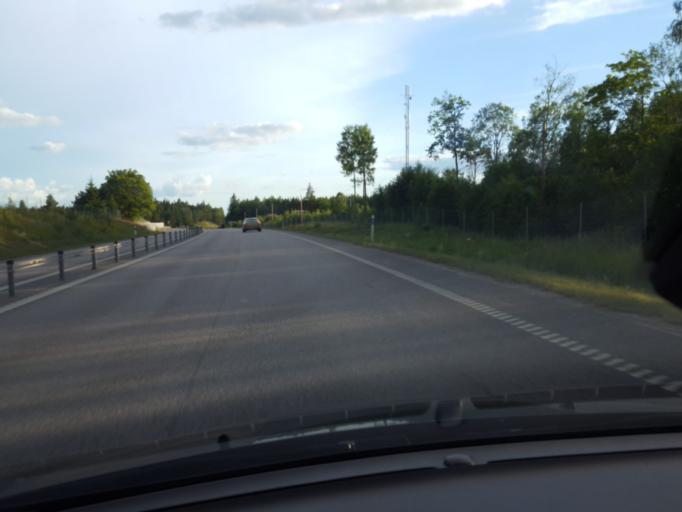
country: SE
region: Uppsala
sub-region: Uppsala Kommun
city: Storvreta
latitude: 59.9211
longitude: 17.7619
